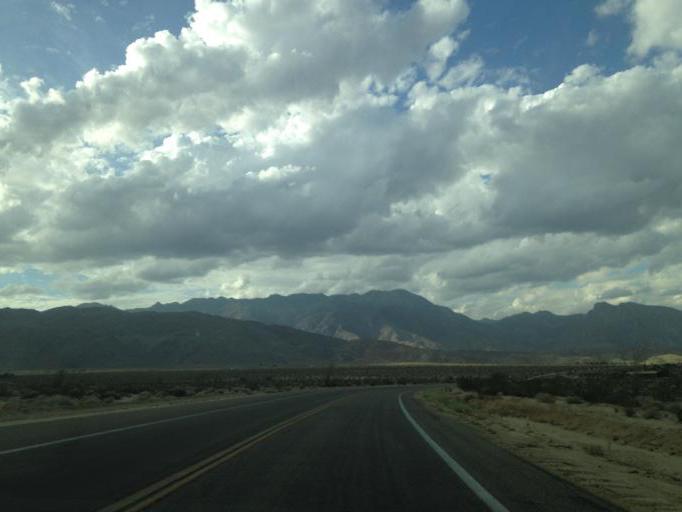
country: US
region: California
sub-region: San Diego County
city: Borrego Springs
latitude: 33.2124
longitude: -116.3673
